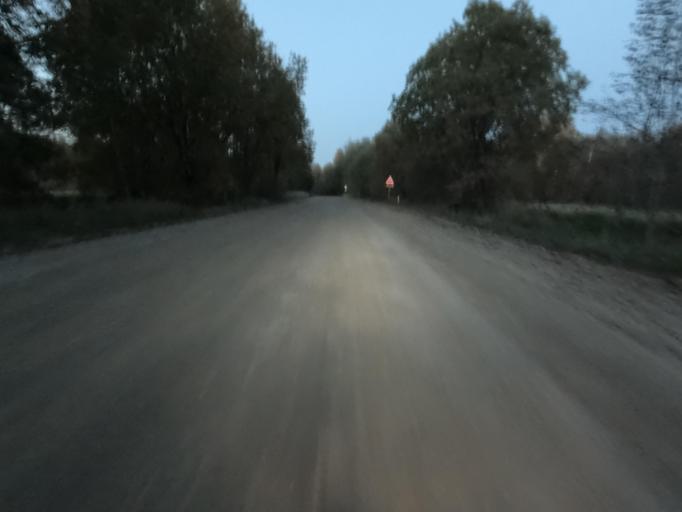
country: RU
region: Leningrad
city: Lyuban'
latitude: 59.1871
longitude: 31.2484
